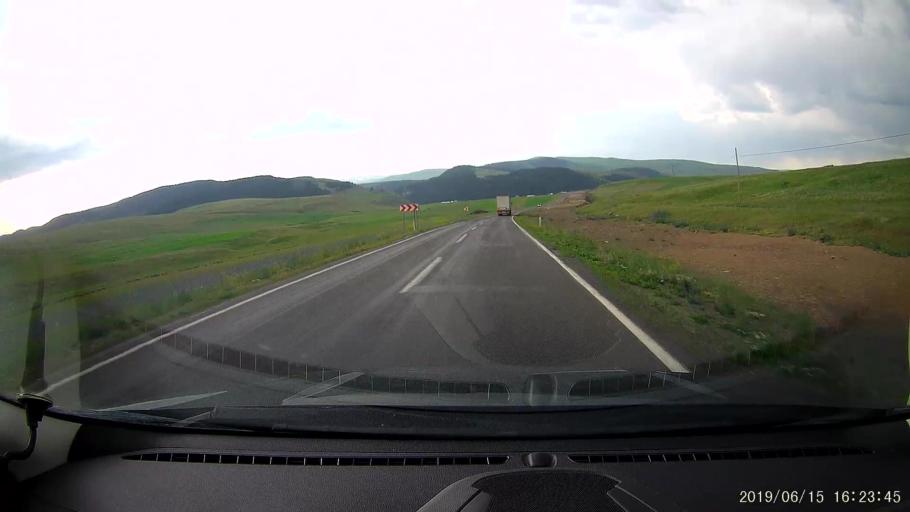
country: TR
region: Ardahan
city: Hanak
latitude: 41.1741
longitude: 42.8652
